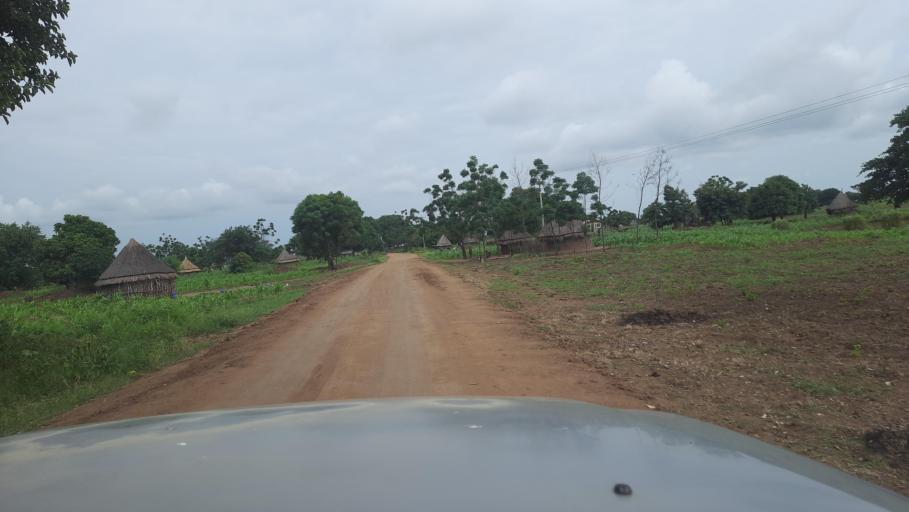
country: ET
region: Gambela
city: Gambela
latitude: 8.3277
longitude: 33.7107
